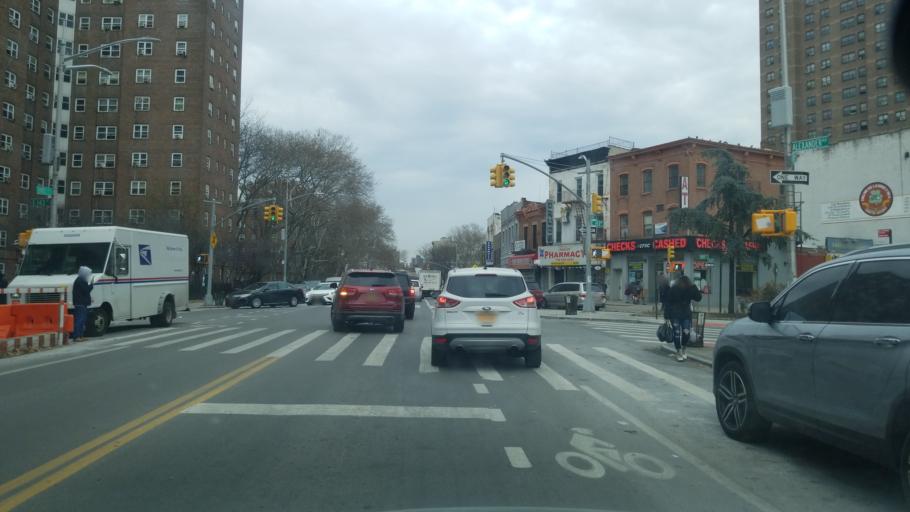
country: US
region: New York
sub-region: New York County
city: Manhattan
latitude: 40.8132
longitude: -73.9231
